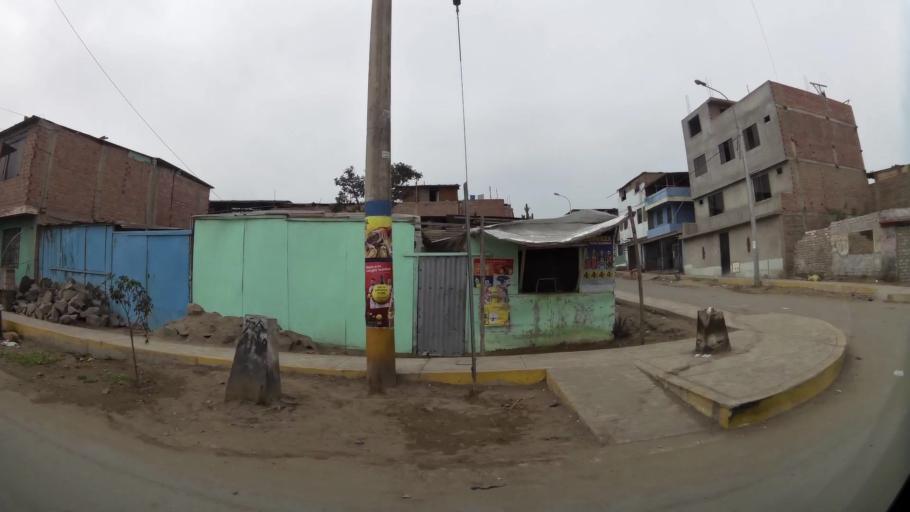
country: PE
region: Lima
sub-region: Lima
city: Surco
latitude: -12.2222
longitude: -76.9452
